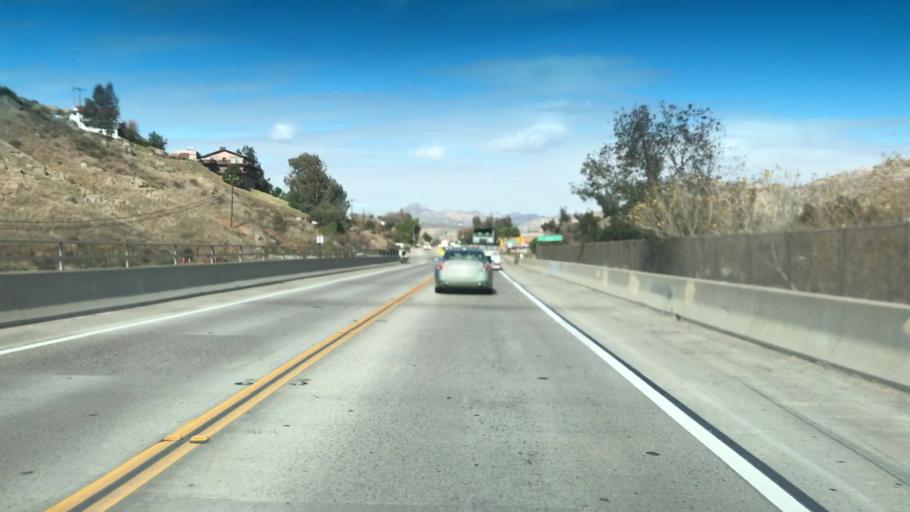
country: US
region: California
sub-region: San Diego County
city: Lakeside
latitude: 32.8703
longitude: -116.9233
